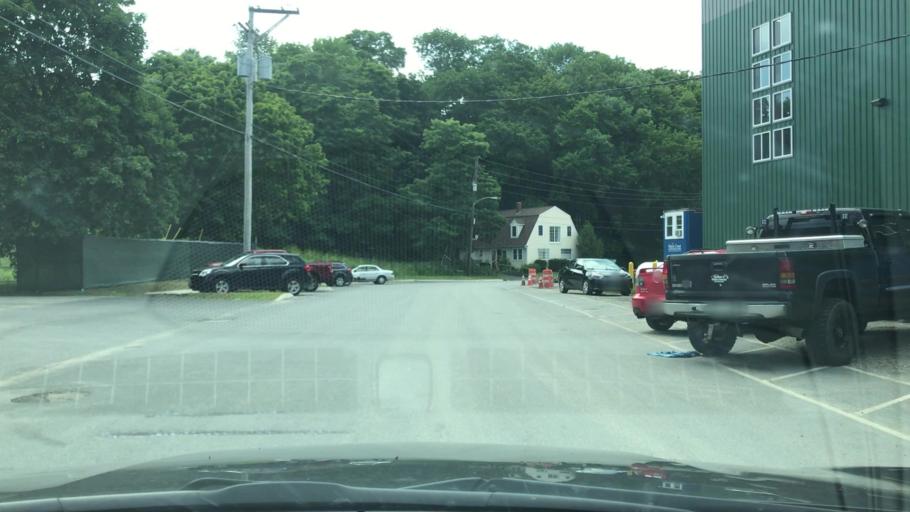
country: US
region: Maine
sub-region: Waldo County
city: Belfast
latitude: 44.4282
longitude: -69.0069
